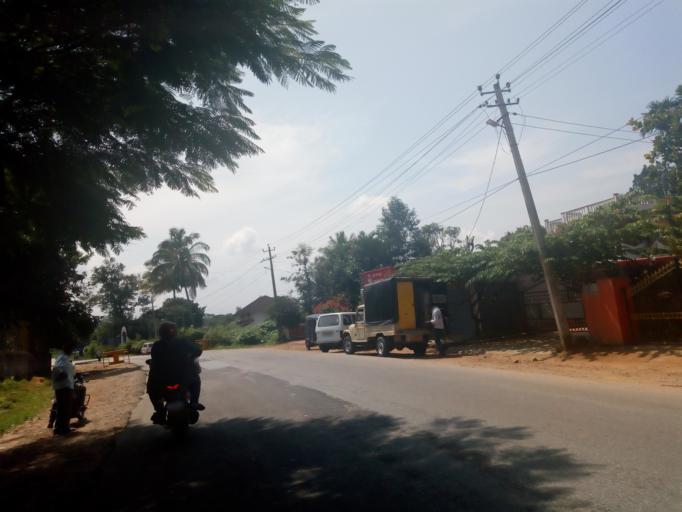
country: IN
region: Karnataka
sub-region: Kodagu
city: Ponnampet
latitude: 12.1358
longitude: 75.9438
